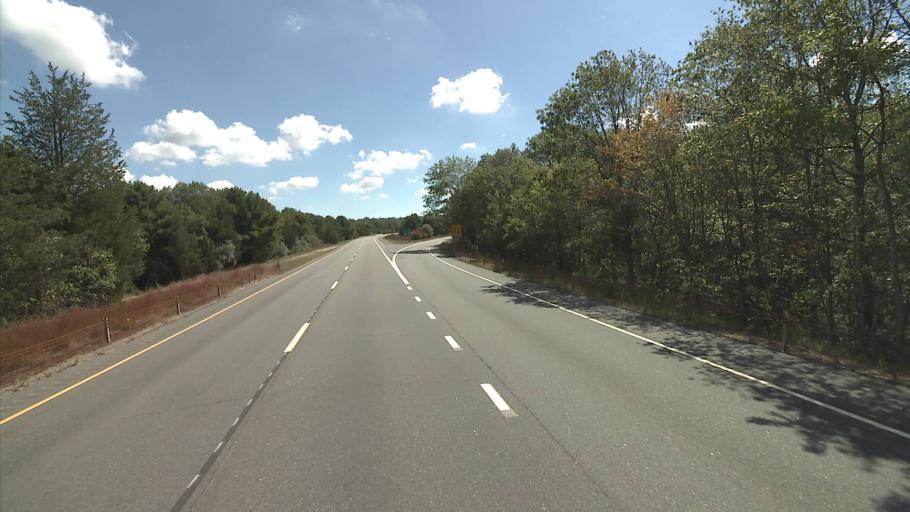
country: US
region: Connecticut
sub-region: New London County
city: Colchester
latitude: 41.5612
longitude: -72.3255
